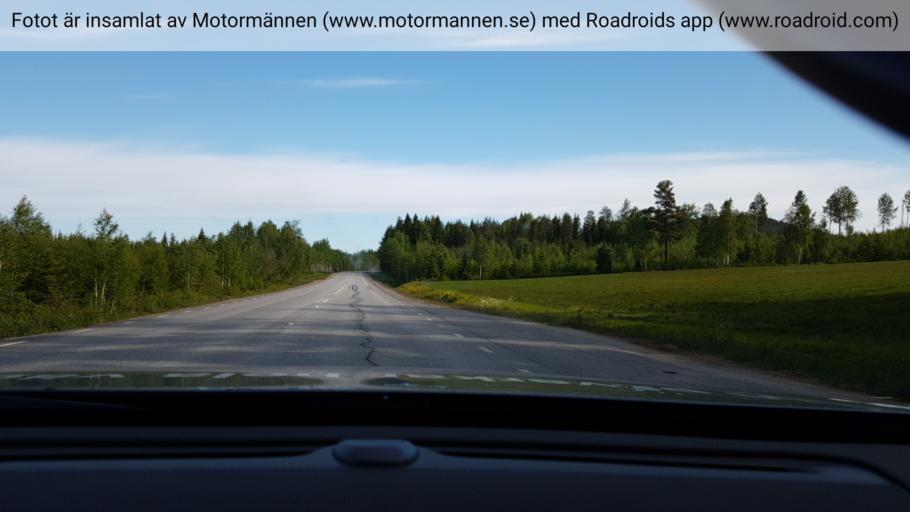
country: SE
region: Vaesterbotten
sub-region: Vannas Kommun
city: Vaennaes
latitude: 63.9302
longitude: 19.7725
